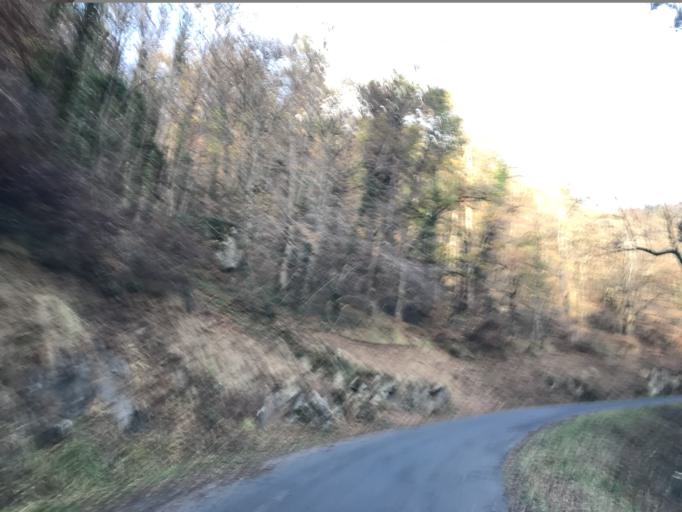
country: FR
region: Auvergne
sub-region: Departement du Puy-de-Dome
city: Courpiere
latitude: 45.7595
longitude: 3.6246
